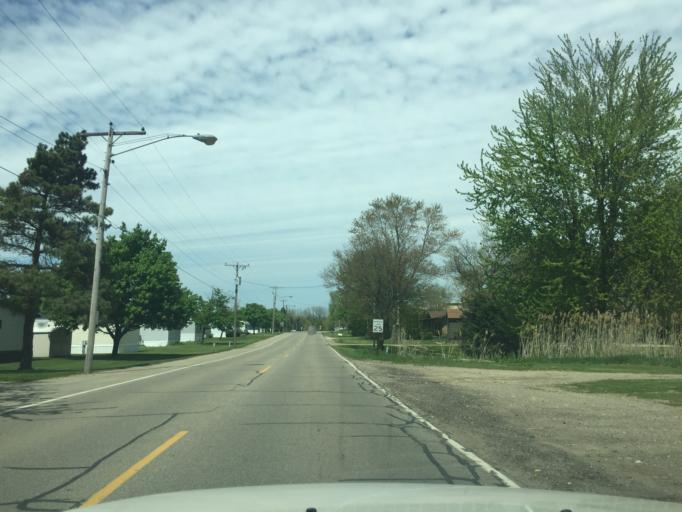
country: US
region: Michigan
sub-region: Berrien County
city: Stevensville
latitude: 41.9578
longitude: -86.4859
